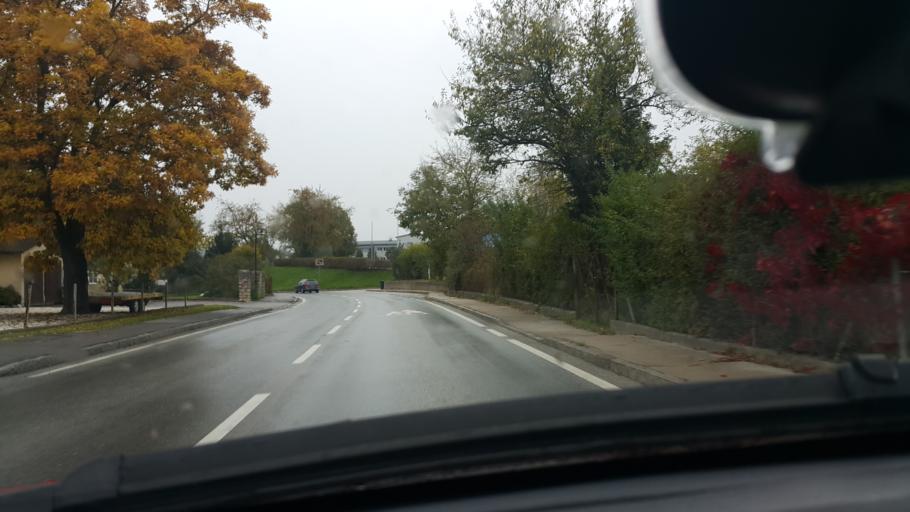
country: AT
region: Carinthia
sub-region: Politischer Bezirk Wolfsberg
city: Lavamund
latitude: 46.6414
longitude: 14.9467
